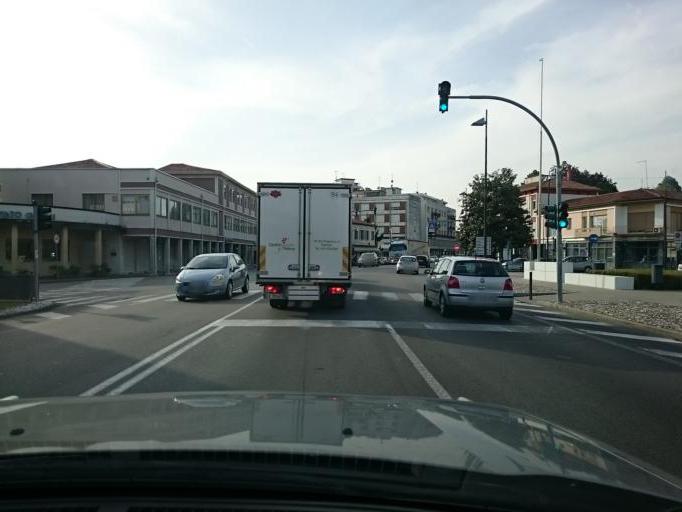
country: IT
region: Veneto
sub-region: Provincia di Padova
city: Oltre Brenta
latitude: 45.4100
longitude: 12.0049
